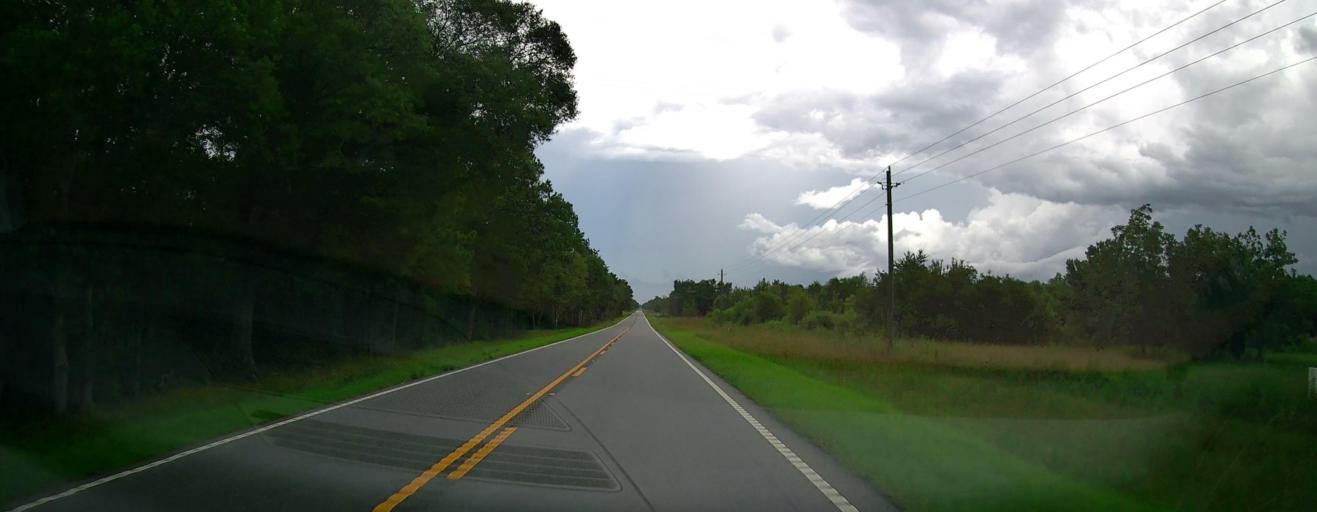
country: US
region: Georgia
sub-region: Pierce County
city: Blackshear
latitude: 31.3699
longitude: -82.1000
